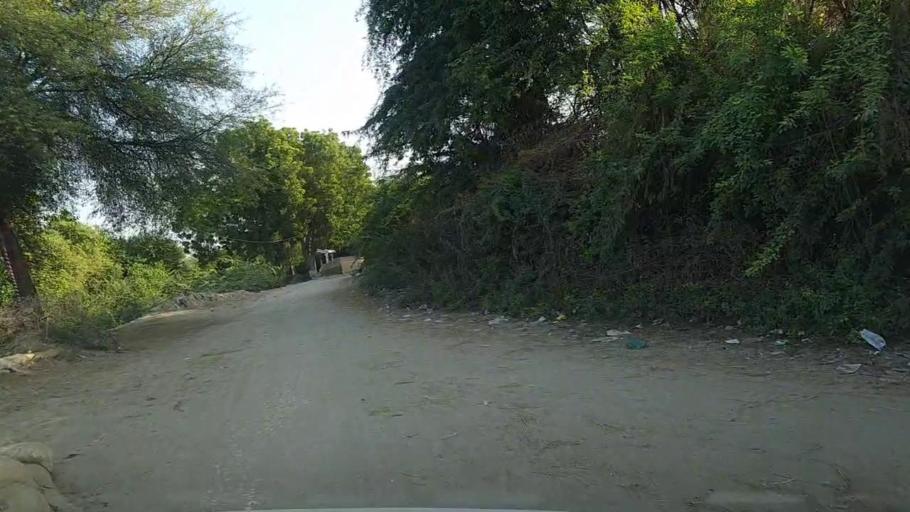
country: PK
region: Sindh
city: Kario
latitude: 24.6904
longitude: 68.6729
